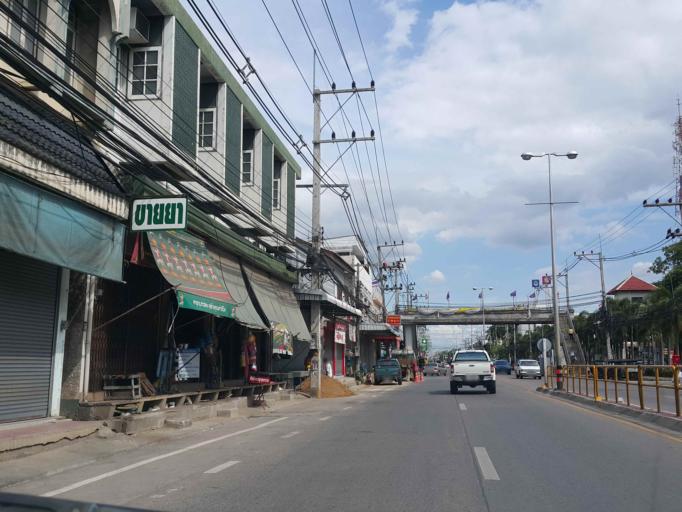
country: TH
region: Chiang Mai
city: San Sai
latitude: 18.9153
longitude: 98.9451
